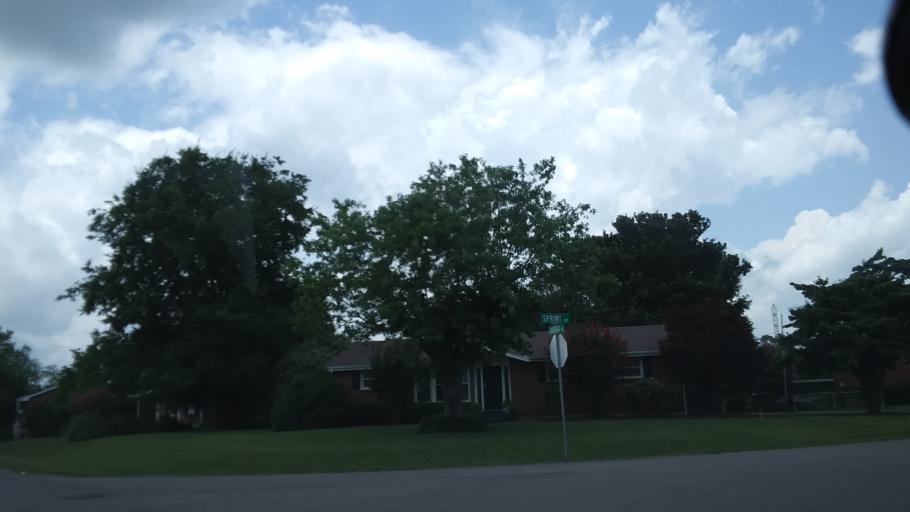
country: US
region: Tennessee
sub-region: Davidson County
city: Belle Meade
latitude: 36.1444
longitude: -86.8870
